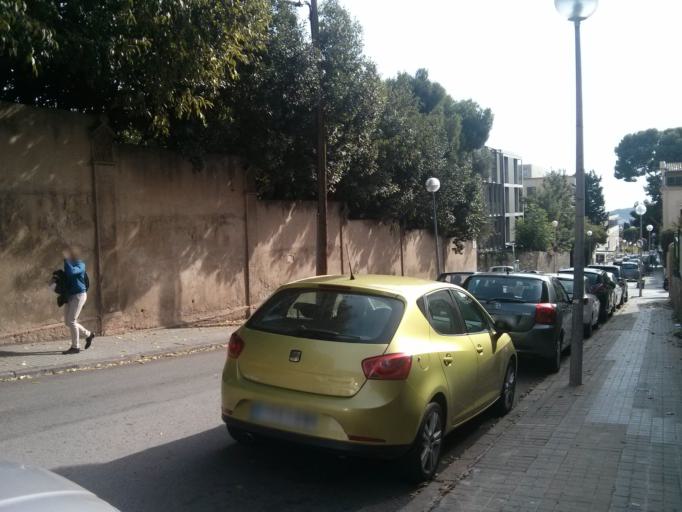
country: ES
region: Catalonia
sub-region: Provincia de Barcelona
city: Sarria-Sant Gervasi
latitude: 41.4076
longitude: 2.1251
